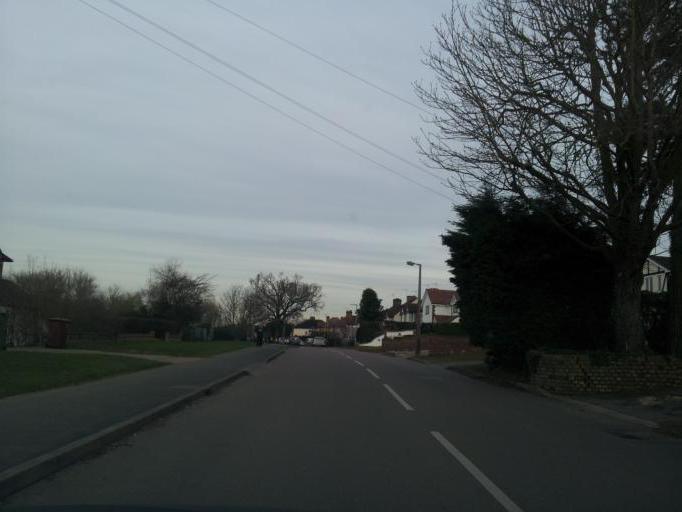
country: GB
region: England
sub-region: Hertfordshire
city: Bushey
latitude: 51.6474
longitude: -0.3508
